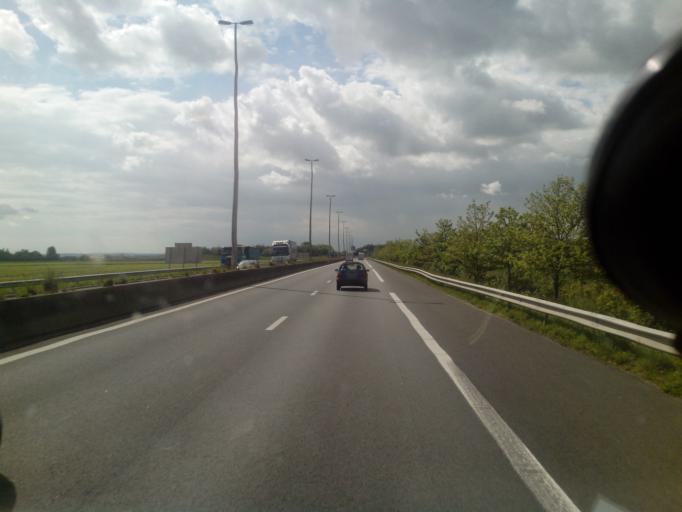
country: FR
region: Nord-Pas-de-Calais
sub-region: Departement du Pas-de-Calais
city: Marck
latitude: 50.9351
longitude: 1.9813
